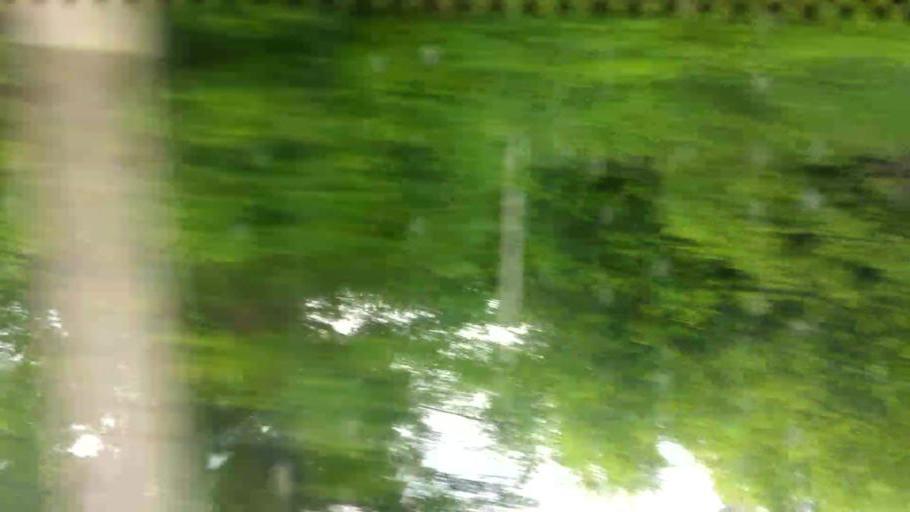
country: RU
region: Moskovskaya
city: Ozherel'ye
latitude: 54.8524
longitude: 38.2408
